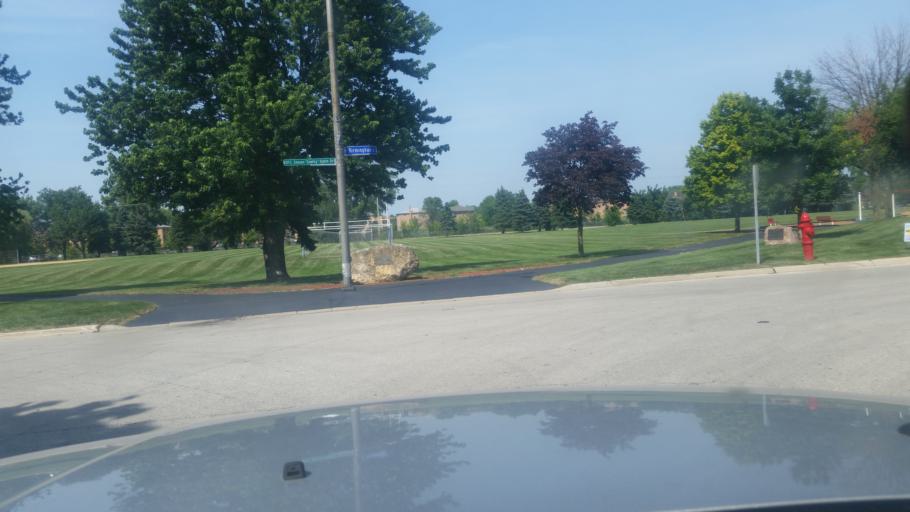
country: US
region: Illinois
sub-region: Cook County
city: Chicago Ridge
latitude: 41.7018
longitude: -87.7749
